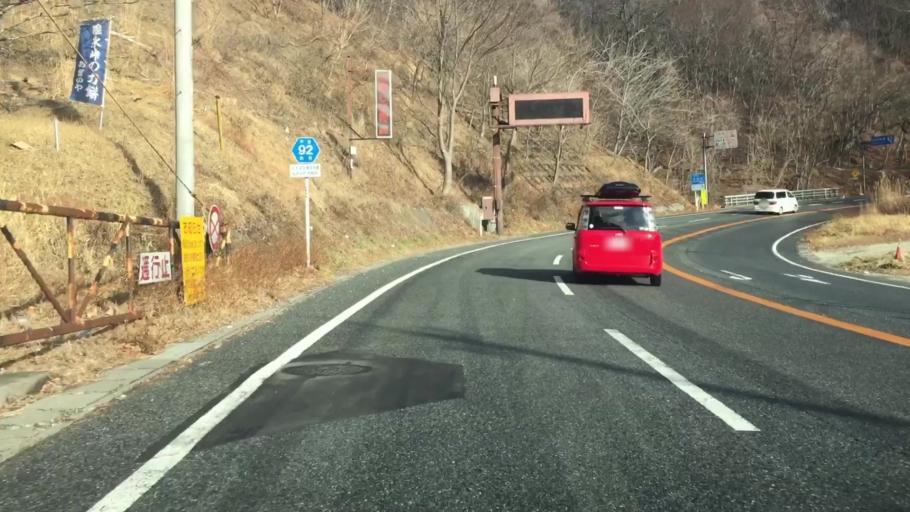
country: JP
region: Nagano
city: Saku
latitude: 36.2993
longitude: 138.6703
